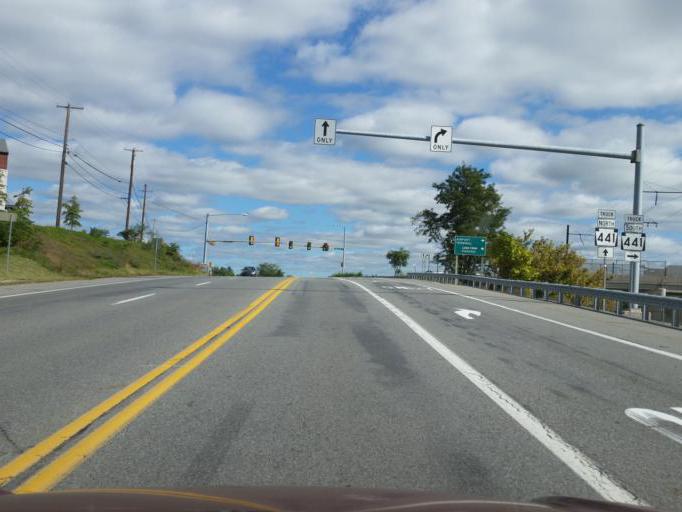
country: US
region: Pennsylvania
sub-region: Dauphin County
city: Middletown
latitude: 40.1967
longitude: -76.7405
